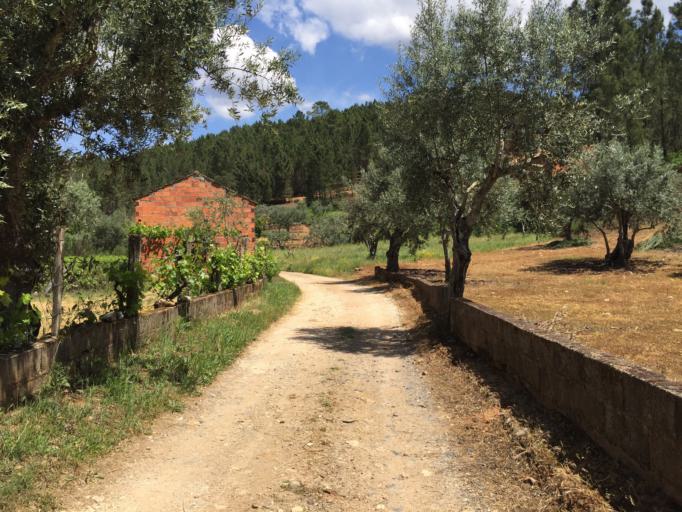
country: PT
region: Coimbra
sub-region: Pampilhosa da Serra
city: Pampilhosa da Serra
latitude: 40.0741
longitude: -7.7852
